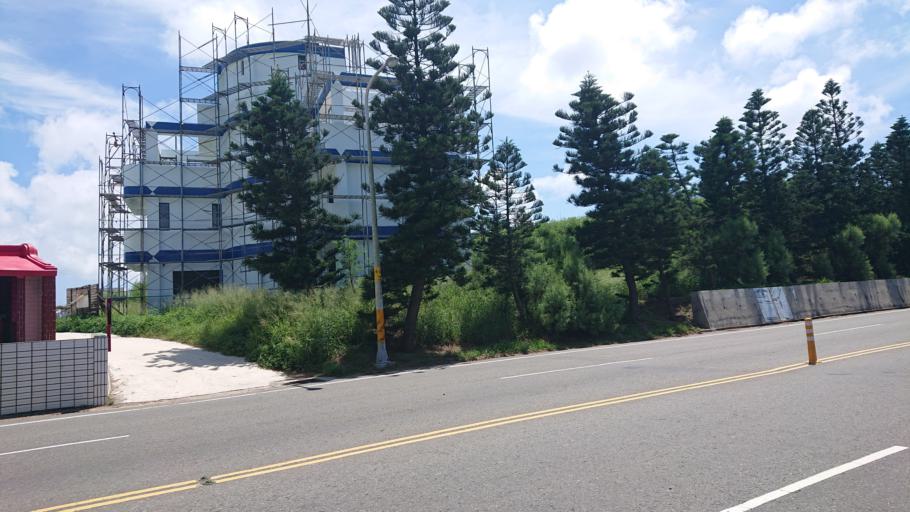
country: TW
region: Taiwan
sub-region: Penghu
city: Ma-kung
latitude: 23.6610
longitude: 119.5595
